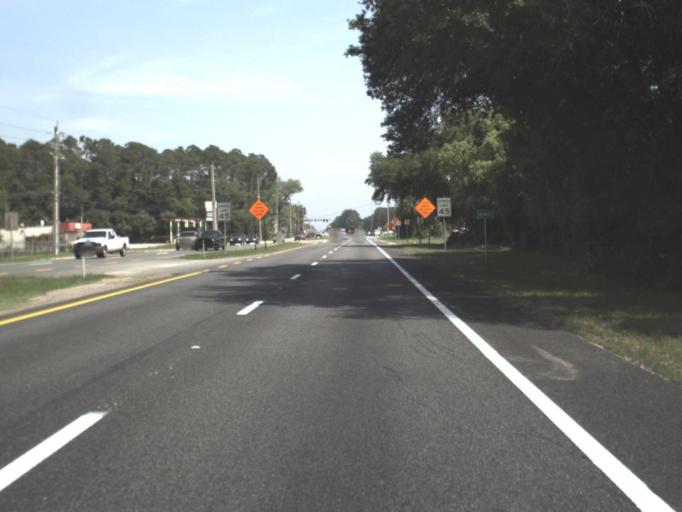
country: US
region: Florida
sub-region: Saint Johns County
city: Fruit Cove
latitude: 30.1464
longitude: -81.5211
